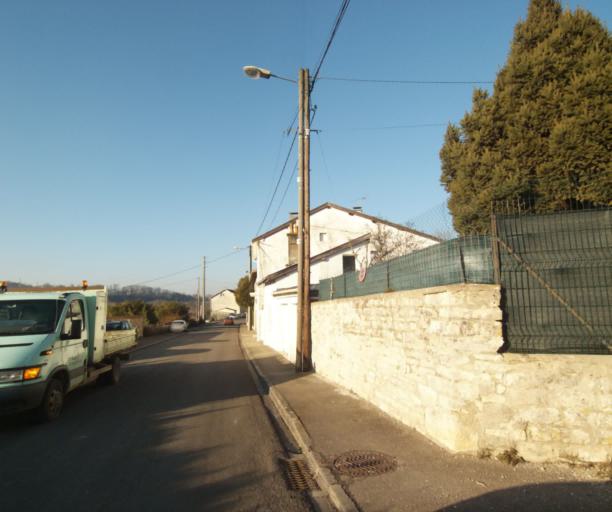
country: FR
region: Champagne-Ardenne
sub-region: Departement de la Haute-Marne
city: Bienville
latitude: 48.5701
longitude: 5.0470
